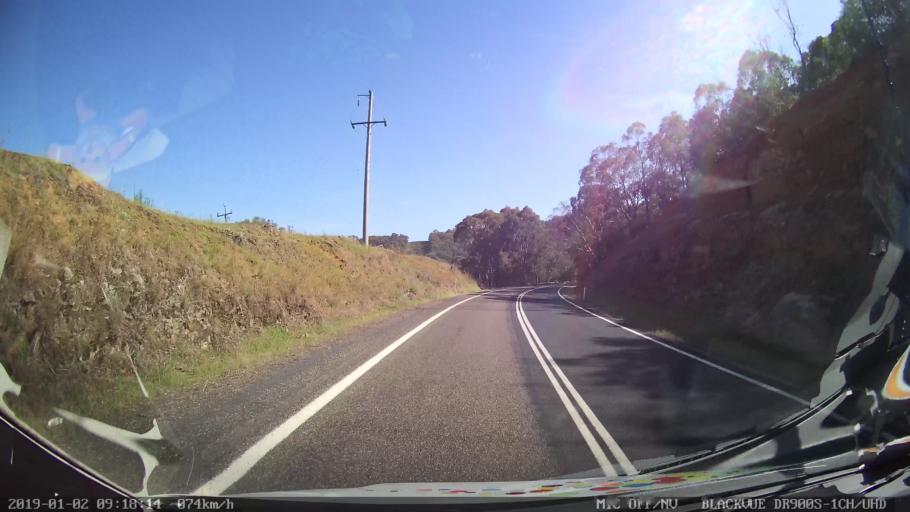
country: AU
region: New South Wales
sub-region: Tumut Shire
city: Tumut
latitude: -35.4311
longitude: 148.2854
